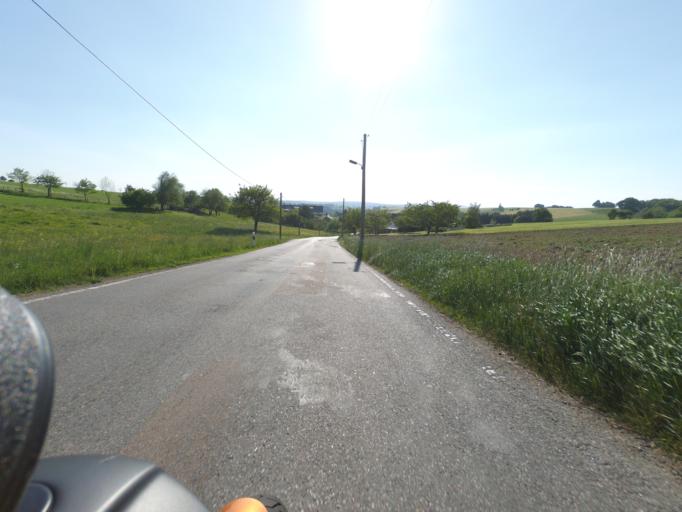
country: DE
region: Saxony
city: Rabenau
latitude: 50.9724
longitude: 13.6749
